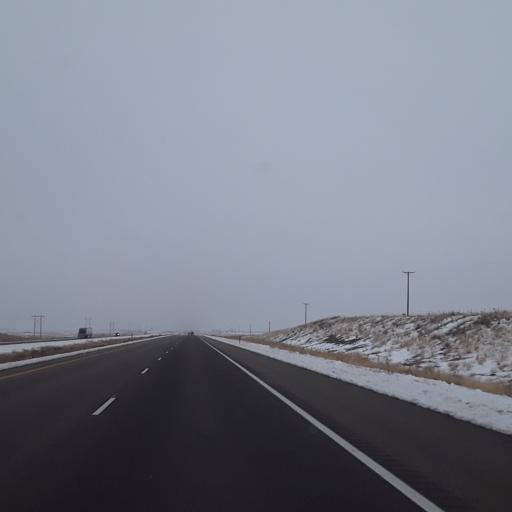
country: US
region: Colorado
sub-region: Logan County
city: Sterling
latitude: 40.4793
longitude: -103.2802
